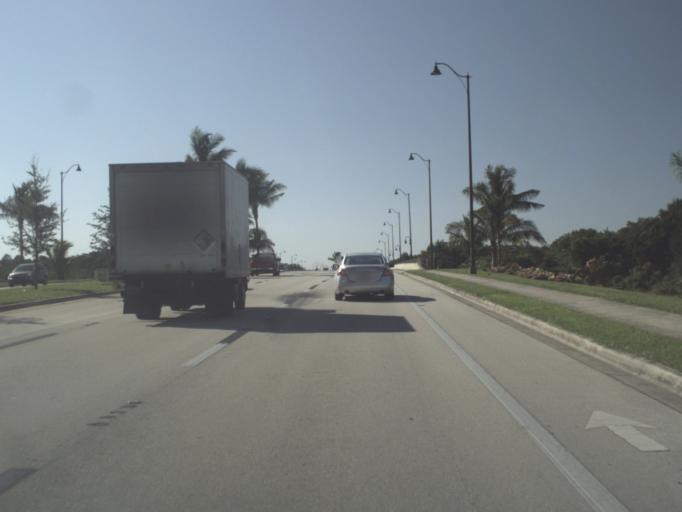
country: US
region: Florida
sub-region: Lee County
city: Bonita Springs
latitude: 26.3411
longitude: -81.8070
